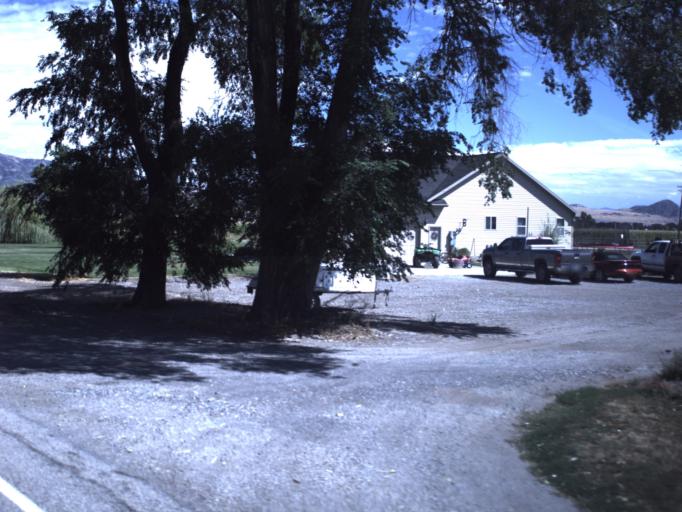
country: US
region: Utah
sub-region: Box Elder County
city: Garland
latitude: 41.7914
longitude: -112.1495
